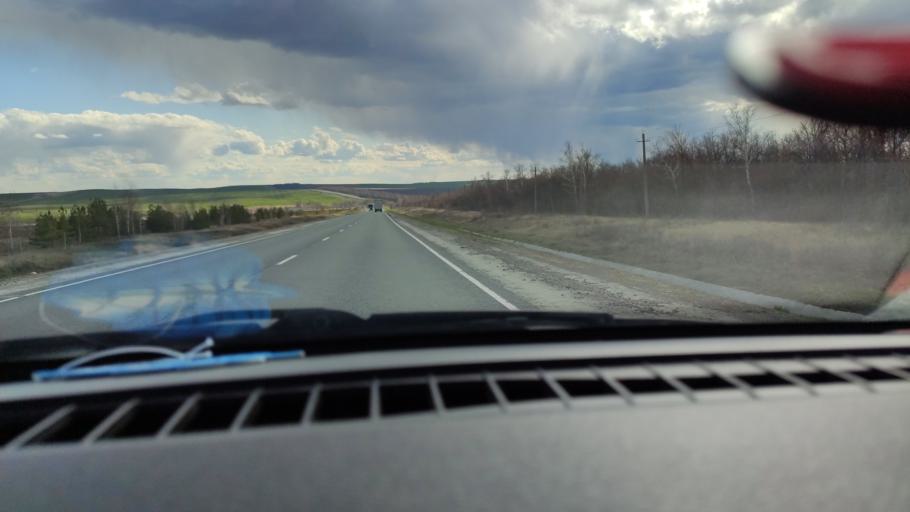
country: RU
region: Saratov
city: Alekseyevka
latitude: 52.2559
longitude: 47.9166
